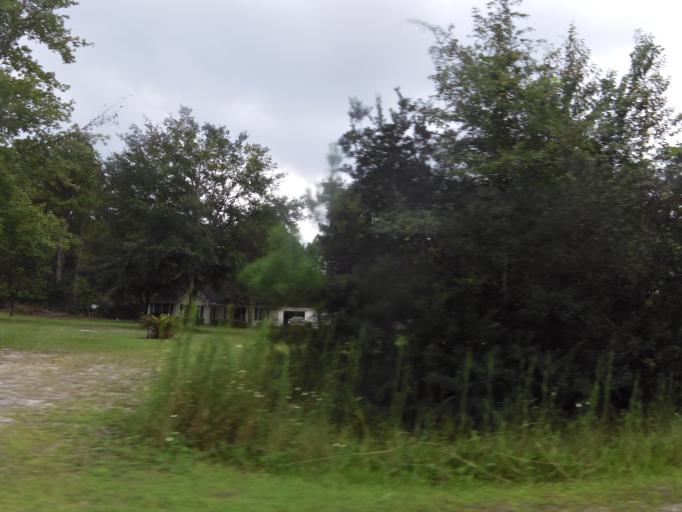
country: US
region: Florida
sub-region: Clay County
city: Middleburg
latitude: 30.1211
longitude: -81.9493
